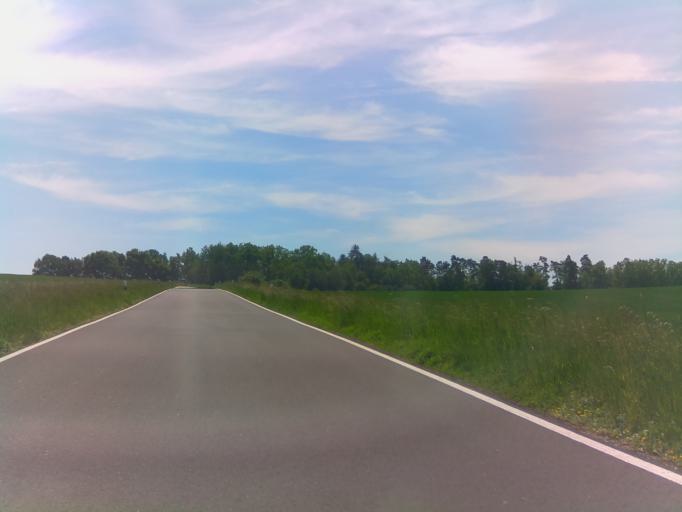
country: DE
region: Thuringia
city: Plaue
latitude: 50.7514
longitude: 10.9441
